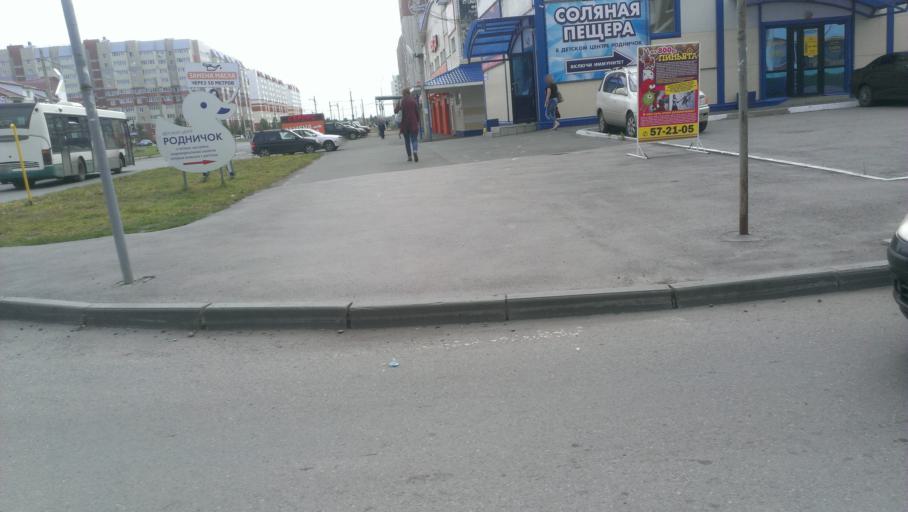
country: RU
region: Altai Krai
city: Novosilikatnyy
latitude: 53.3307
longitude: 83.6756
